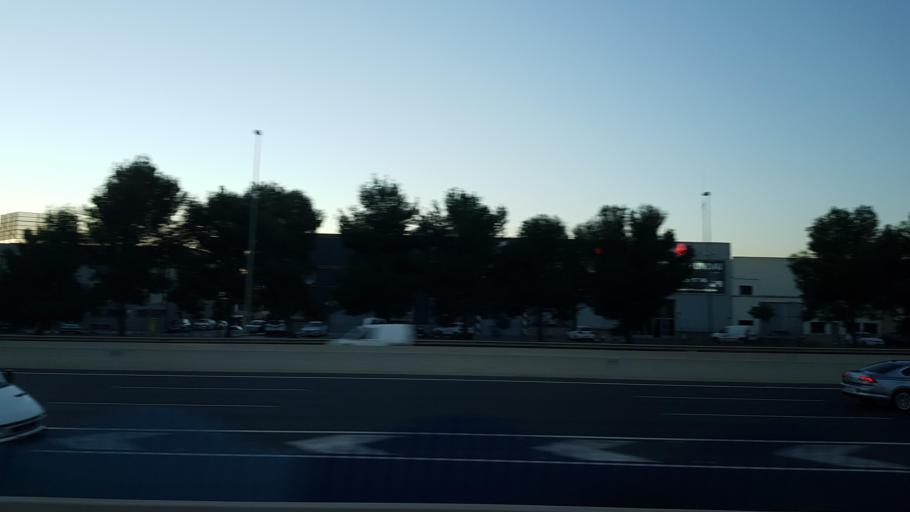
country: ES
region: Valencia
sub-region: Provincia de Valencia
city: Manises
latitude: 39.4784
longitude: -0.4759
